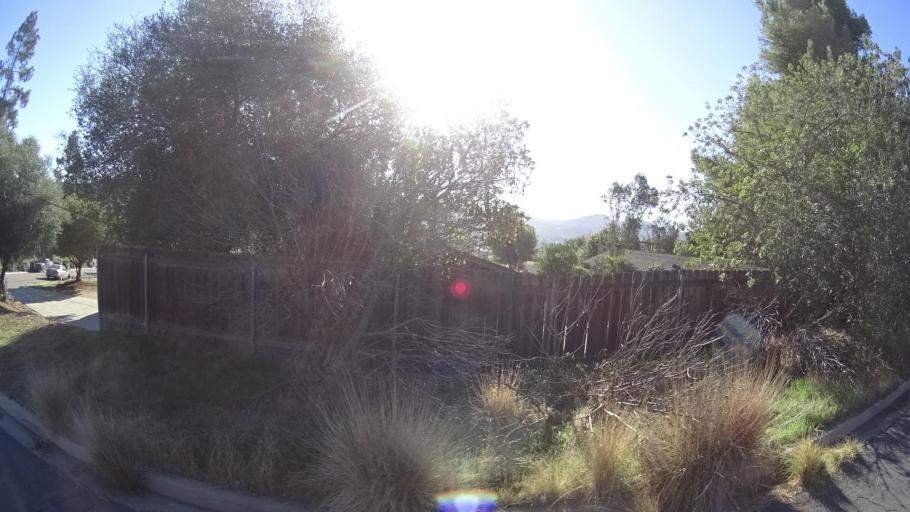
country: US
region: California
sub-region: San Diego County
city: Lakeside
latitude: 32.8458
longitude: -116.9094
